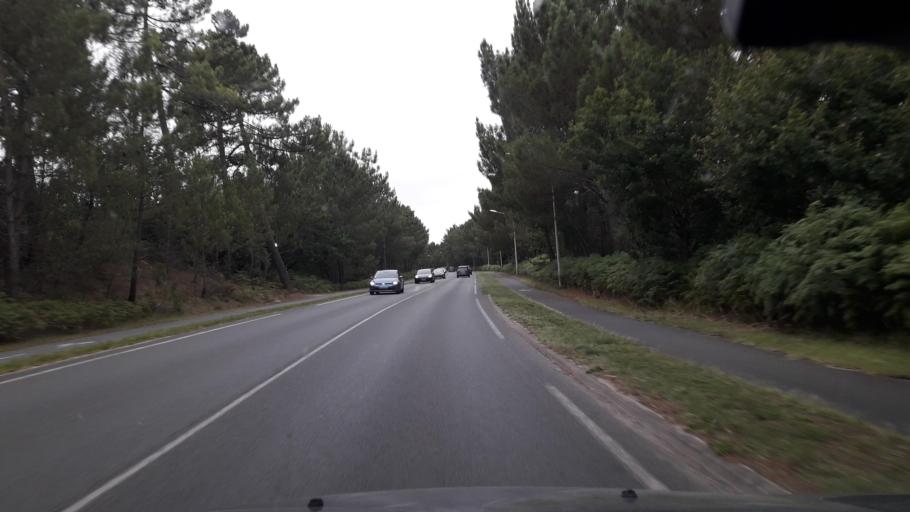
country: FR
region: Poitou-Charentes
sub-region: Departement de la Charente-Maritime
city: Les Mathes
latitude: 45.7086
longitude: -1.1602
